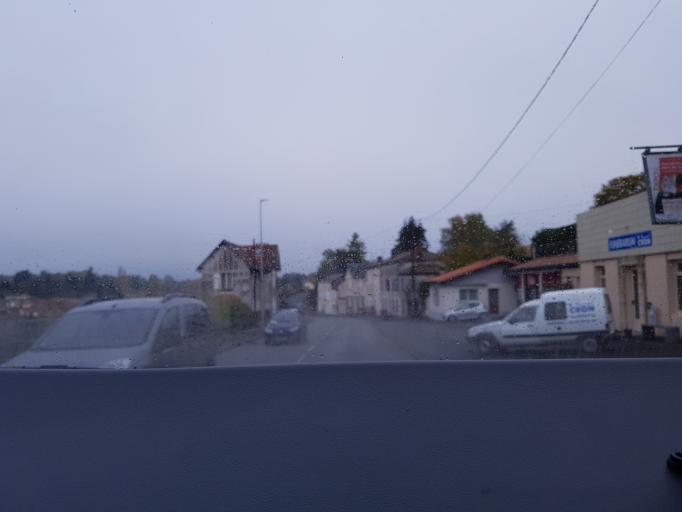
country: FR
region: Poitou-Charentes
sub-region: Departement des Deux-Sevres
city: Parthenay
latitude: 46.6510
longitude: -0.2466
